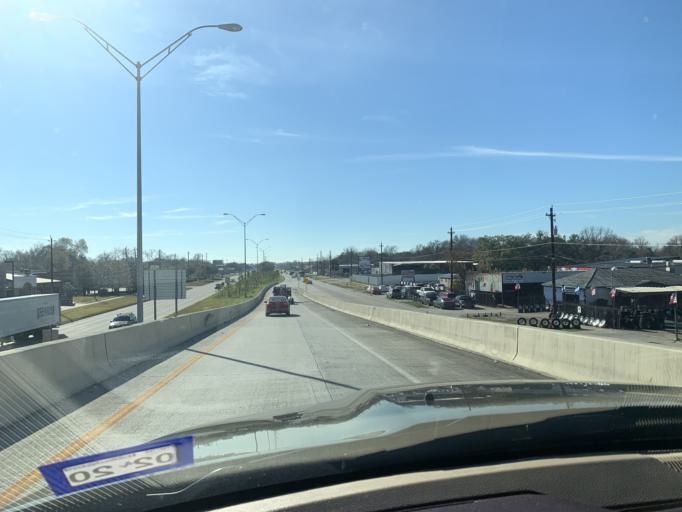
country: US
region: Texas
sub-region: Harris County
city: Aldine
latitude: 29.8683
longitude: -95.4126
